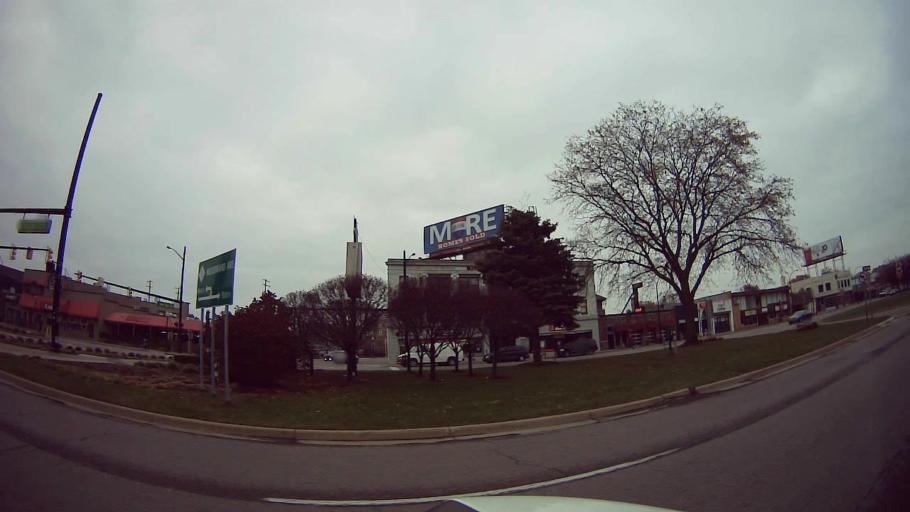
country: US
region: Michigan
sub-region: Oakland County
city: Ferndale
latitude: 42.4602
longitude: -83.1348
